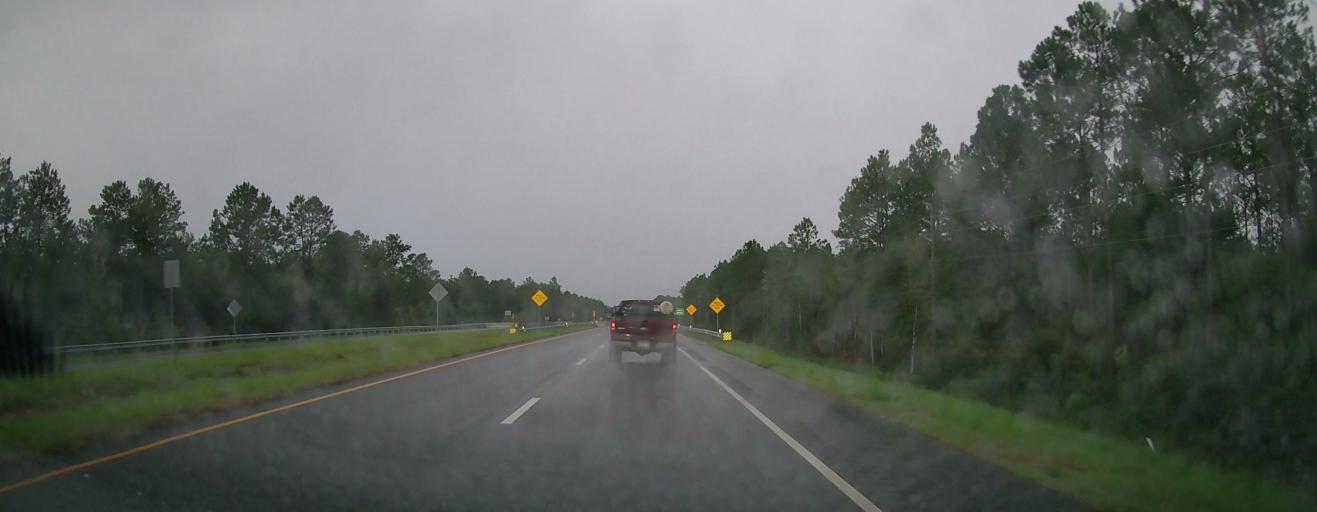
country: US
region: Georgia
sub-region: Clinch County
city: Homerville
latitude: 31.0663
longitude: -82.6688
